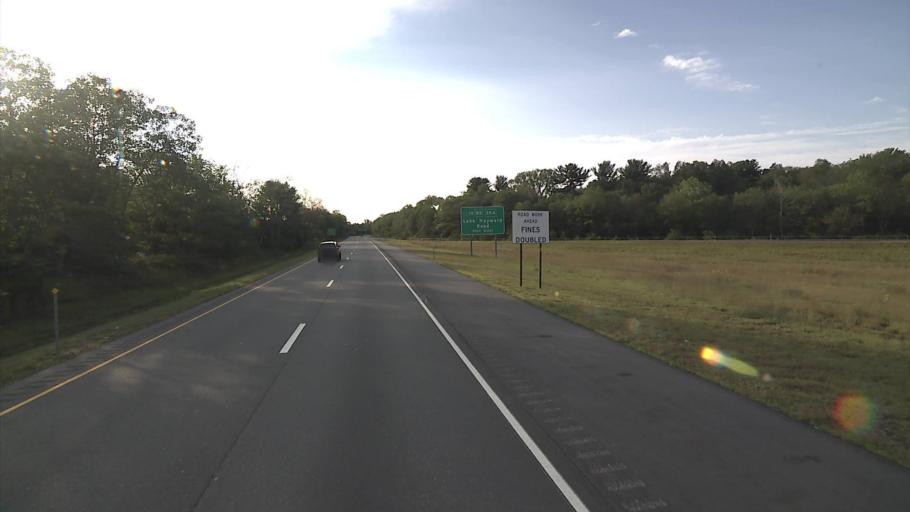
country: US
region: Connecticut
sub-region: New London County
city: Colchester
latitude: 41.5692
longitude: -72.3368
